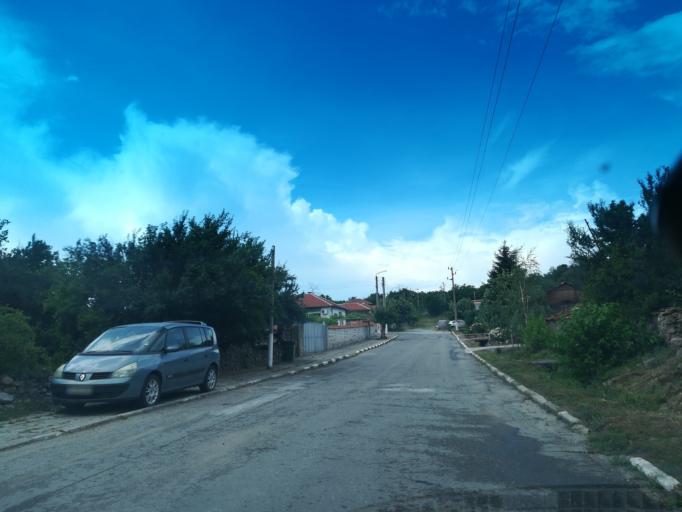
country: BG
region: Khaskovo
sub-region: Obshtina Mineralni Bani
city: Mineralni Bani
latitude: 41.9951
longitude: 25.2270
